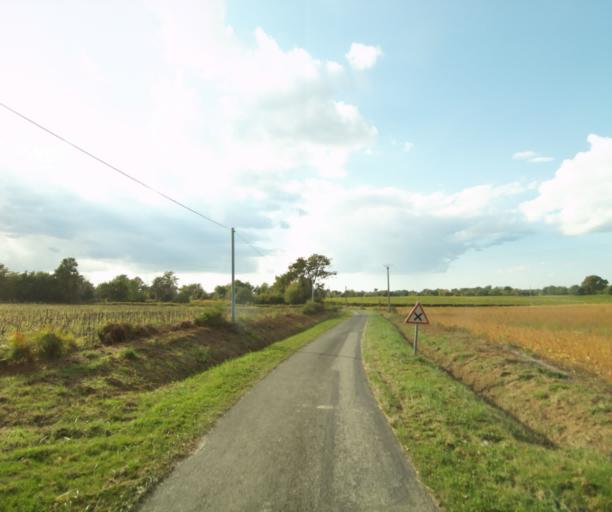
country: FR
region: Midi-Pyrenees
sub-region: Departement du Gers
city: Cazaubon
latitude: 43.9003
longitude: -0.0683
